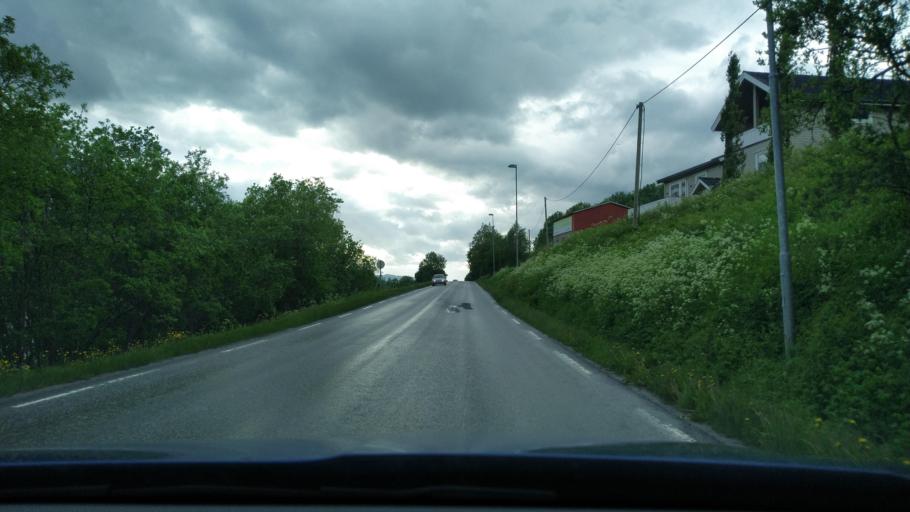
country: NO
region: Troms
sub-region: Balsfjord
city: Storsteinnes
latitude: 69.2209
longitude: 19.5306
